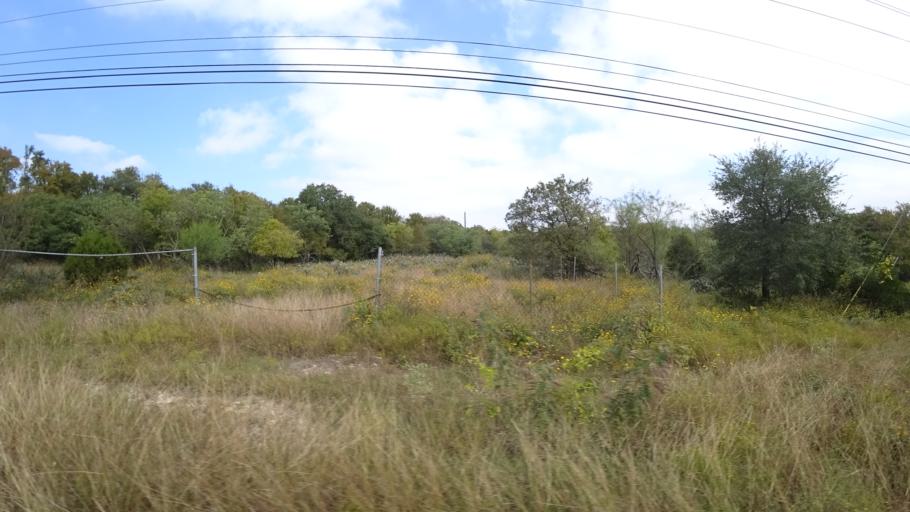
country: US
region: Texas
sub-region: Travis County
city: Shady Hollow
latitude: 30.1938
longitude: -97.8392
